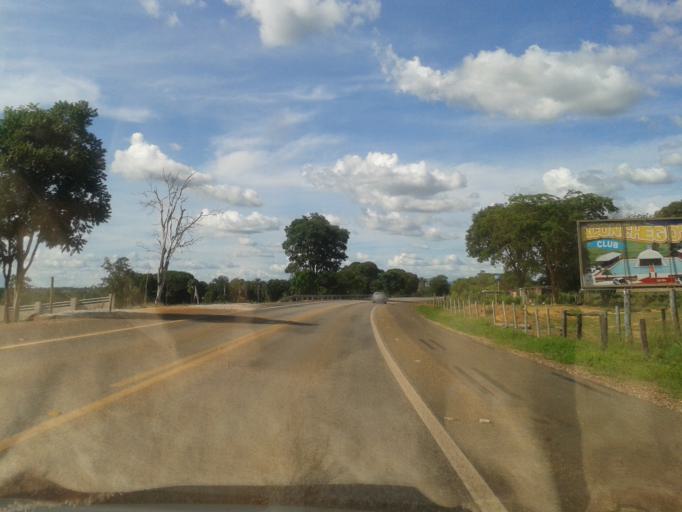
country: BR
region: Goias
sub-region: Mozarlandia
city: Mozarlandia
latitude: -15.0838
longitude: -50.6231
